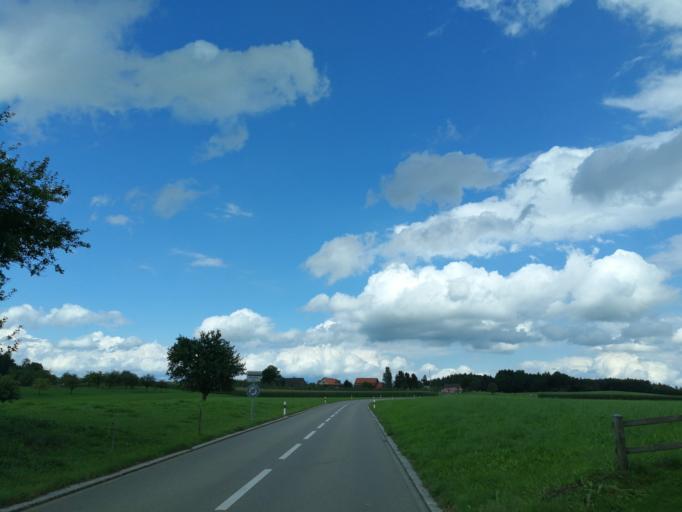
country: CH
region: Thurgau
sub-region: Weinfelden District
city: Sulgen
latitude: 47.5131
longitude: 9.1775
